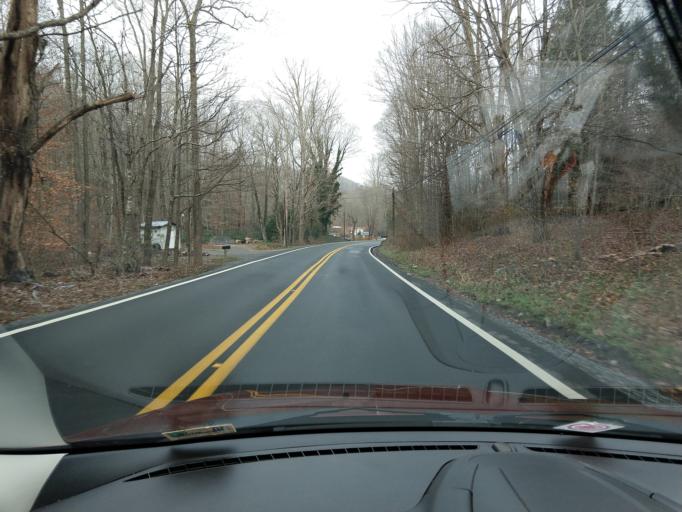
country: US
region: West Virginia
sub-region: Nicholas County
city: Richwood
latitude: 38.1406
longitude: -80.6864
